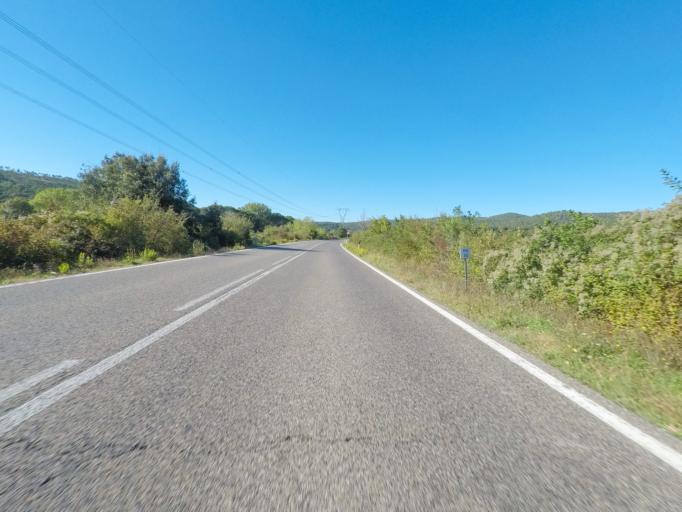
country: IT
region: Tuscany
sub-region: Provincia di Grosseto
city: Civitella Marittima
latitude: 43.0212
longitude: 11.2822
